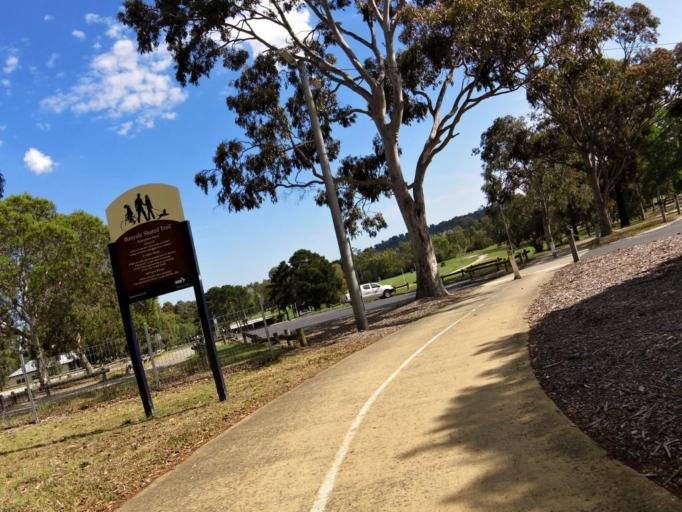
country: AU
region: Victoria
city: Rosanna
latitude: -37.7504
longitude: 145.0792
